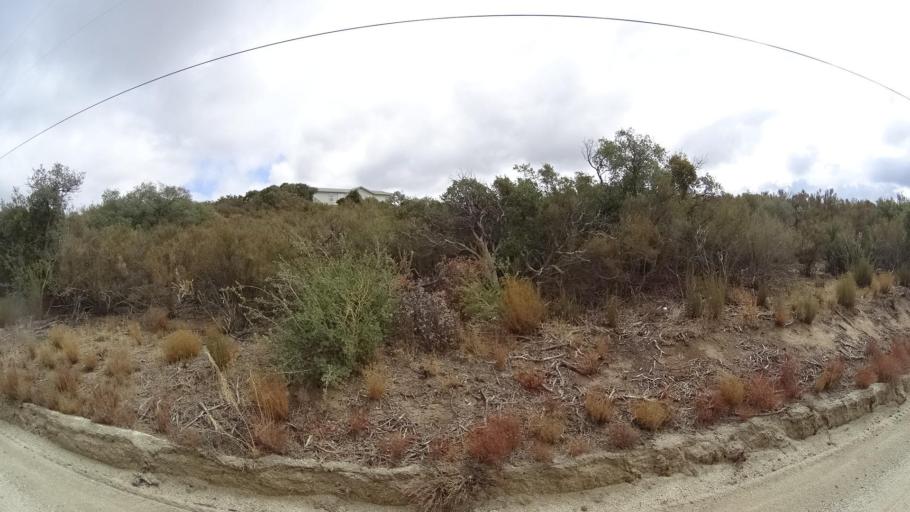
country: US
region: California
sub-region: San Diego County
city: Campo
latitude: 32.7058
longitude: -116.3885
